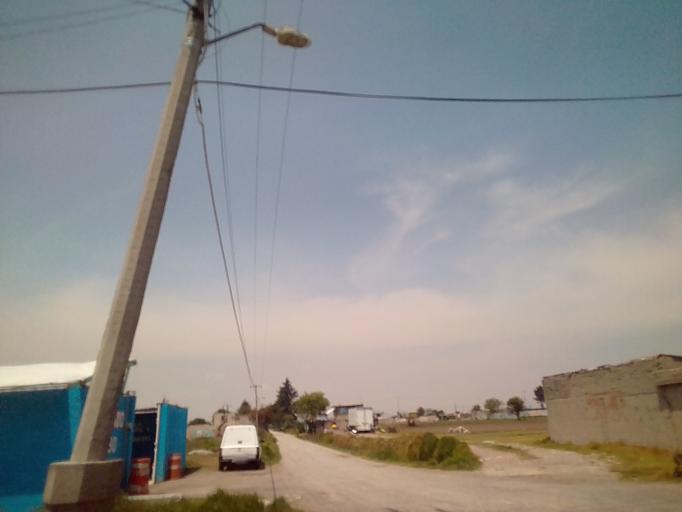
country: MX
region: Mexico
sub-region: Toluca
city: Guadalupe Totoltepec
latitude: 19.3535
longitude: -99.5593
